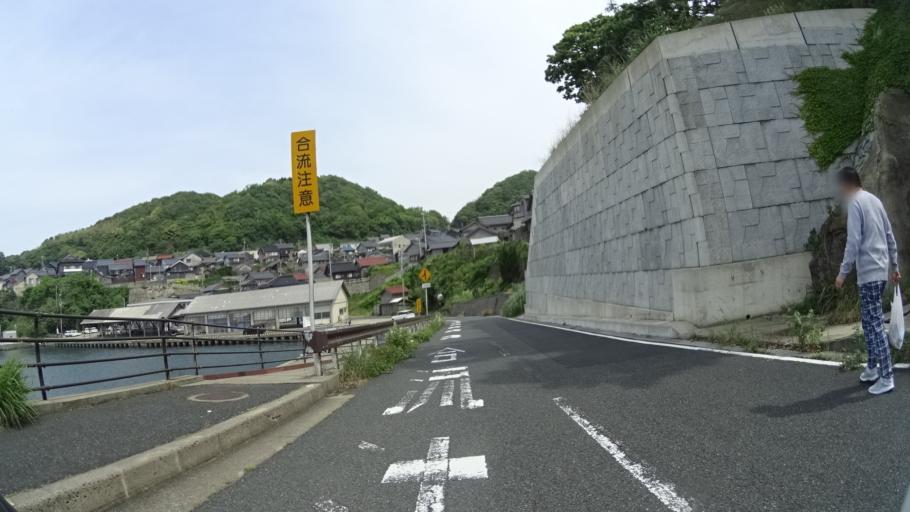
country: JP
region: Kyoto
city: Miyazu
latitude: 35.7385
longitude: 135.0920
